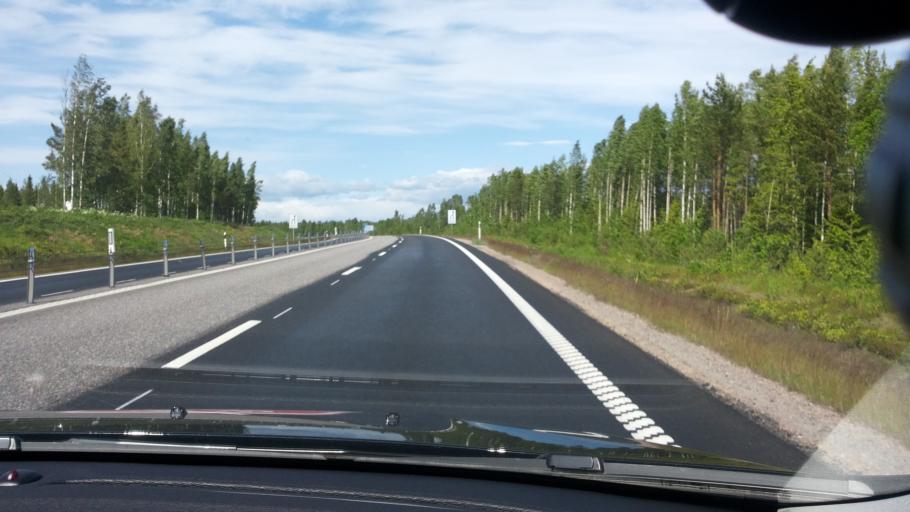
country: SE
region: Vaesternorrland
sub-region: Sundsvalls Kommun
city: Njurundabommen
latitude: 62.1586
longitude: 17.3534
